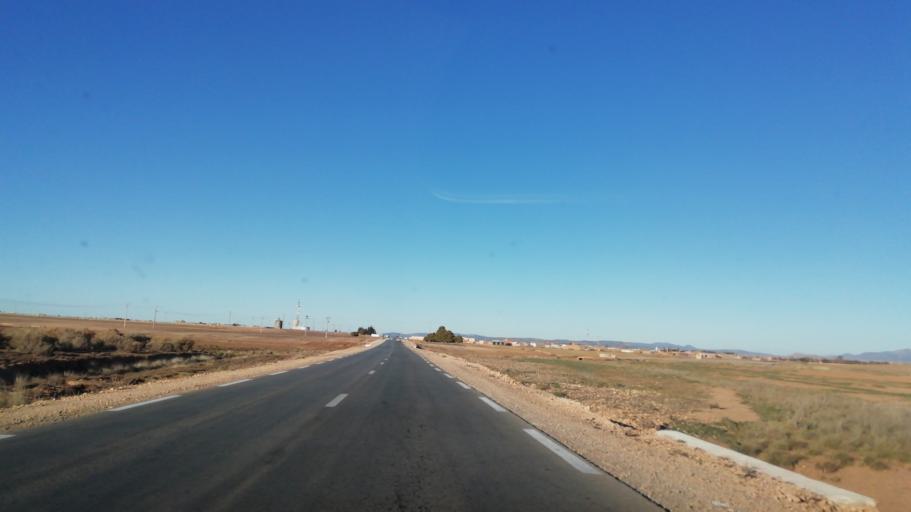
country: DZ
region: Tlemcen
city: Sebdou
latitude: 34.4717
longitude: -1.2720
